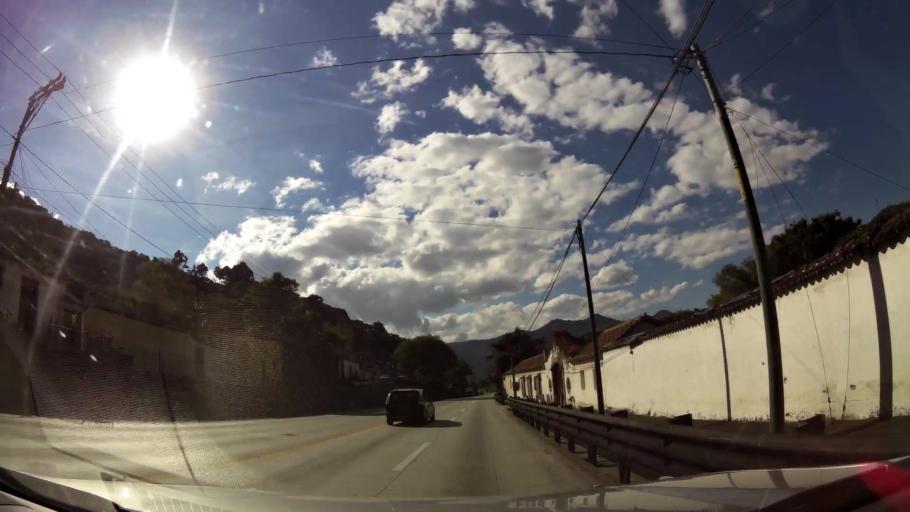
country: GT
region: Sacatepequez
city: Antigua Guatemala
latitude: 14.5584
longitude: -90.7188
